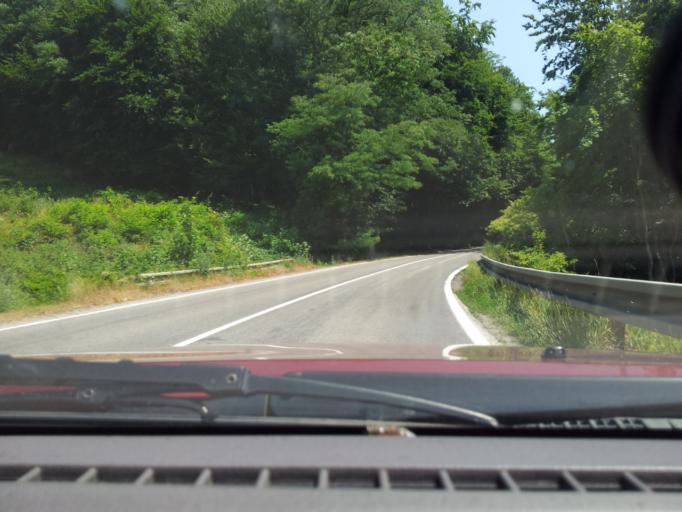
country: SK
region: Trnavsky
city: Smolenice
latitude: 48.5639
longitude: 17.4597
